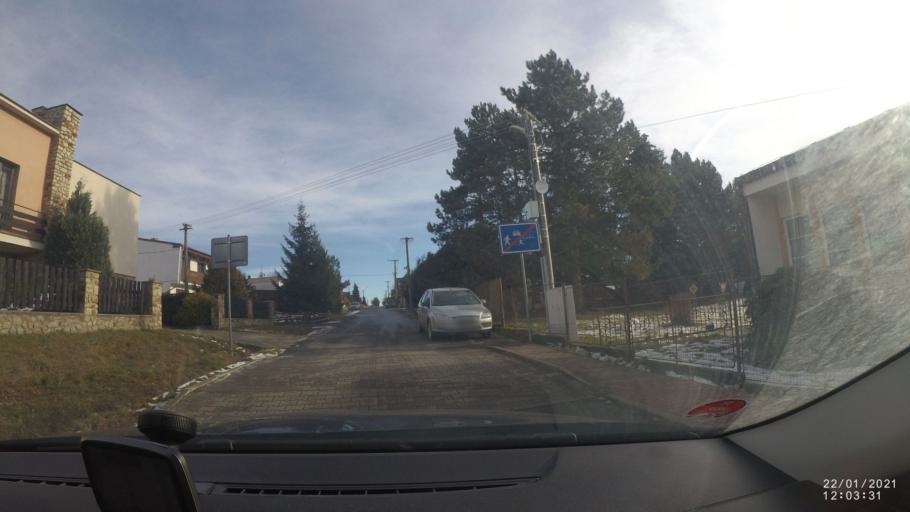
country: CZ
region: Plzensky
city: Dysina
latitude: 49.7478
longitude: 13.5159
